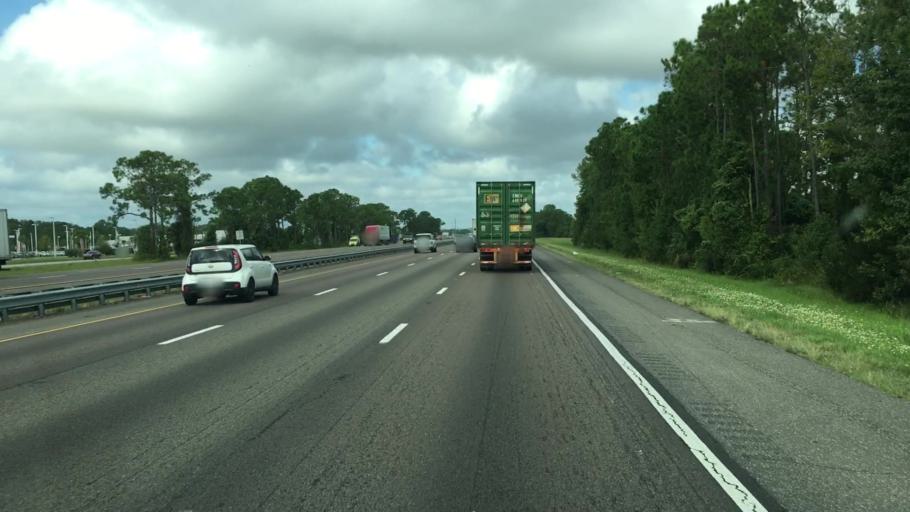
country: US
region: Florida
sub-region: Volusia County
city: Holly Hill
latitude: 29.2016
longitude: -81.0966
